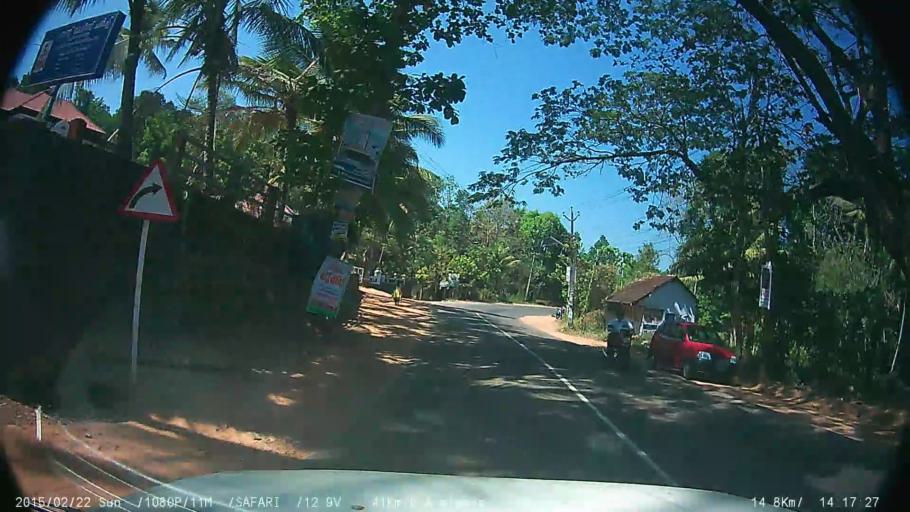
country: IN
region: Kerala
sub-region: Kottayam
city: Lalam
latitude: 9.5618
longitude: 76.6823
